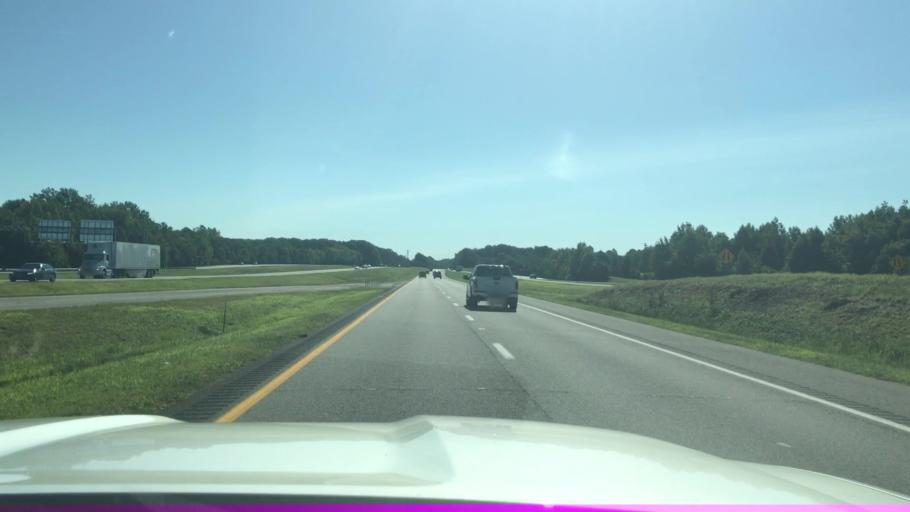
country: US
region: Virginia
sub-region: Henrico County
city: Sandston
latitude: 37.5200
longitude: -77.2672
